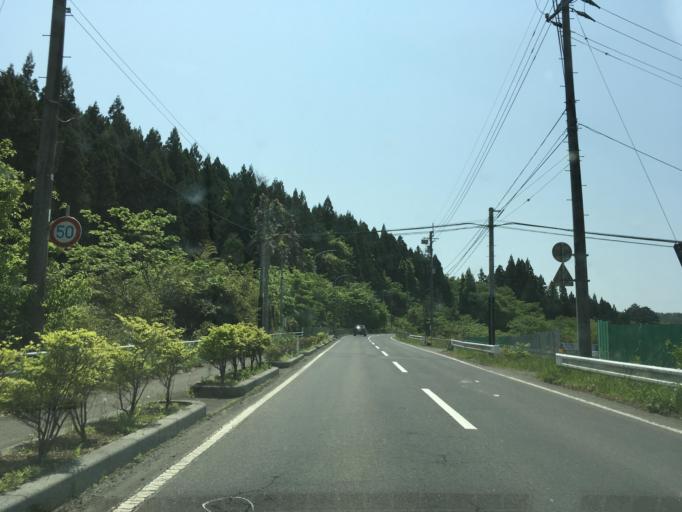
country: JP
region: Iwate
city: Ofunato
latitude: 38.8713
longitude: 141.5368
